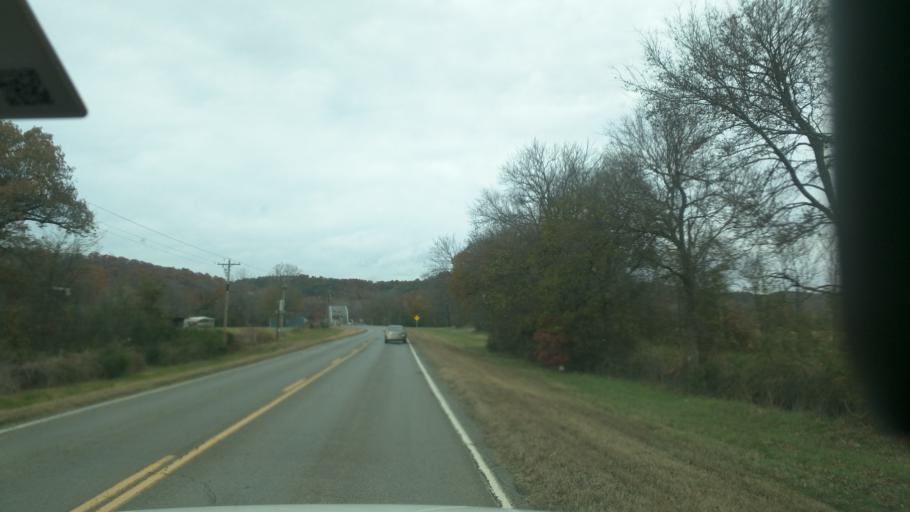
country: US
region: Oklahoma
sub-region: Cherokee County
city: Tahlequah
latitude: 35.9183
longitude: -94.8358
